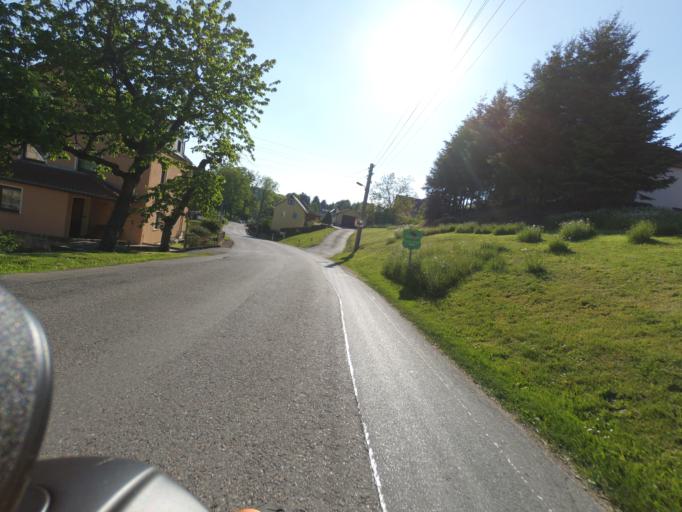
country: DE
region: Saxony
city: Rabenau
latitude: 50.9718
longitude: 13.6610
